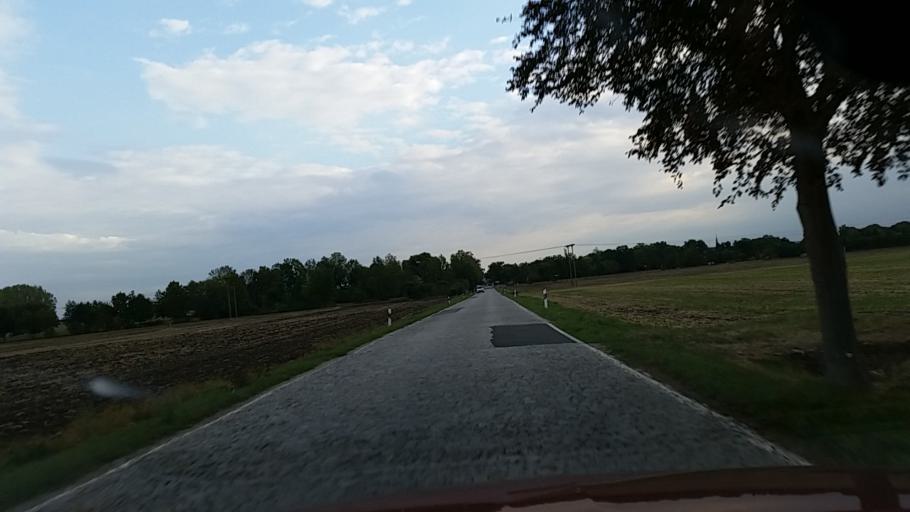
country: DE
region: Thuringia
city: Kolleda
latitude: 51.1982
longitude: 11.2536
